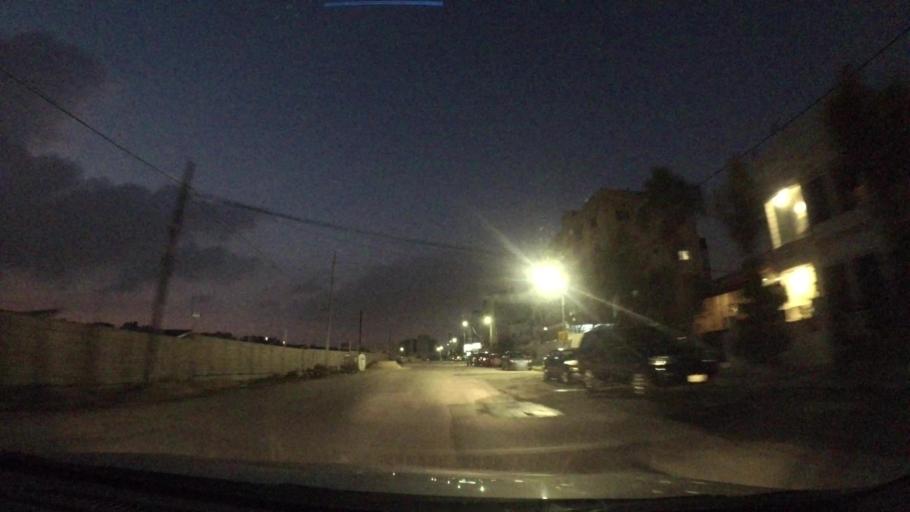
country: JO
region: Amman
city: Al Bunayyat ash Shamaliyah
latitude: 31.9073
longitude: 35.8811
